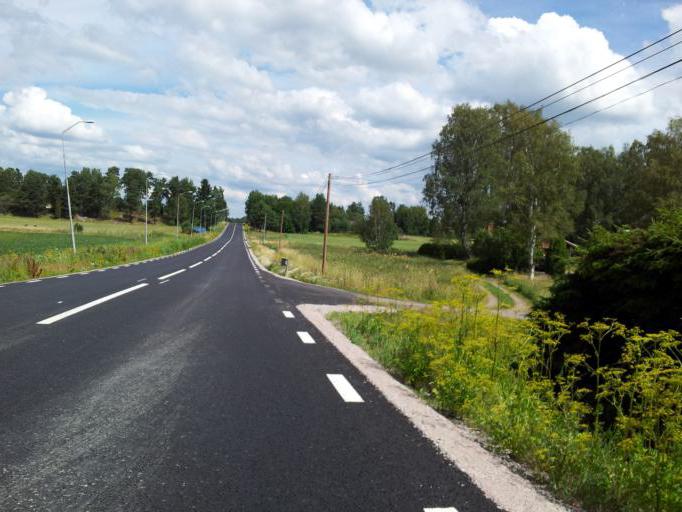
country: SE
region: Stockholm
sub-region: Norrtalje Kommun
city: Nykvarn
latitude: 59.8905
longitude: 18.2218
